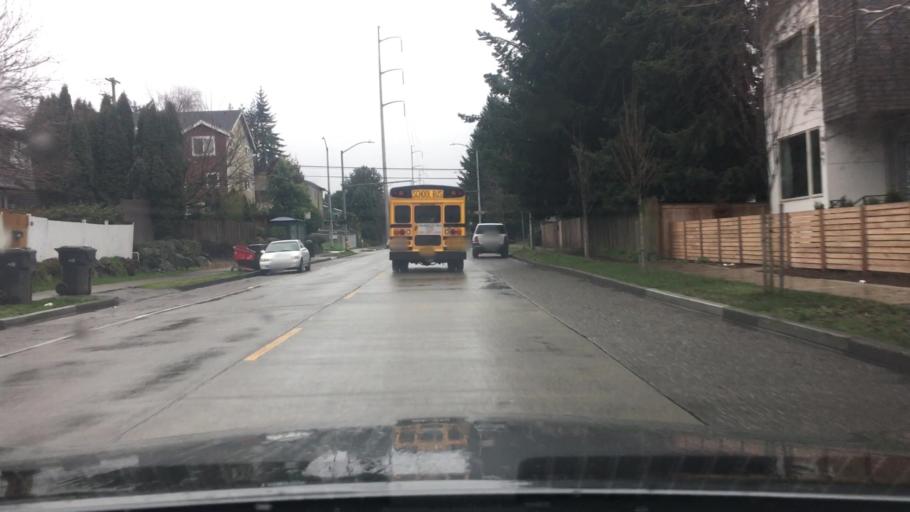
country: US
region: Washington
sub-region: King County
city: White Center
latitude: 47.5291
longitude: -122.3605
